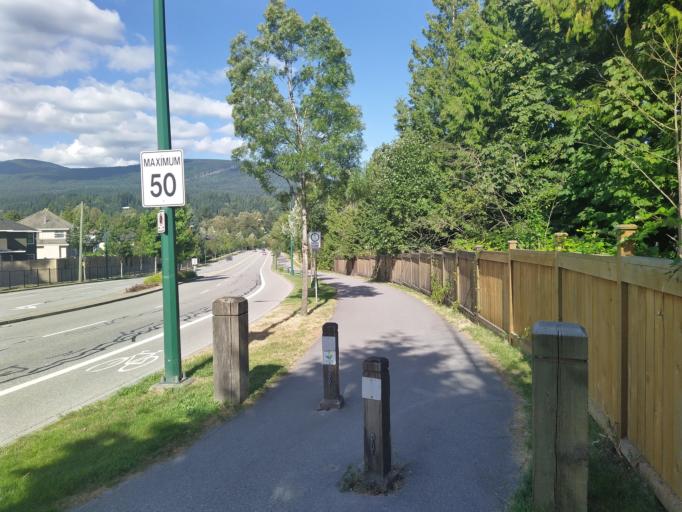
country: CA
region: British Columbia
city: Coquitlam
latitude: 49.2928
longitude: -122.7801
